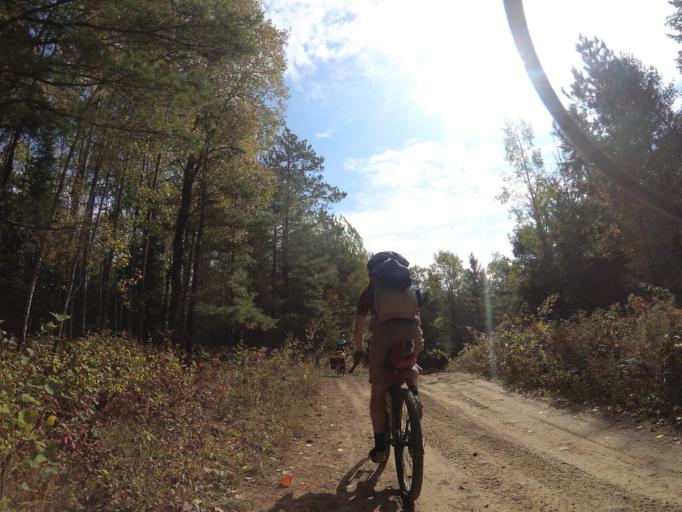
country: CA
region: Ontario
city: Pembroke
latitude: 45.2725
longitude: -77.2159
